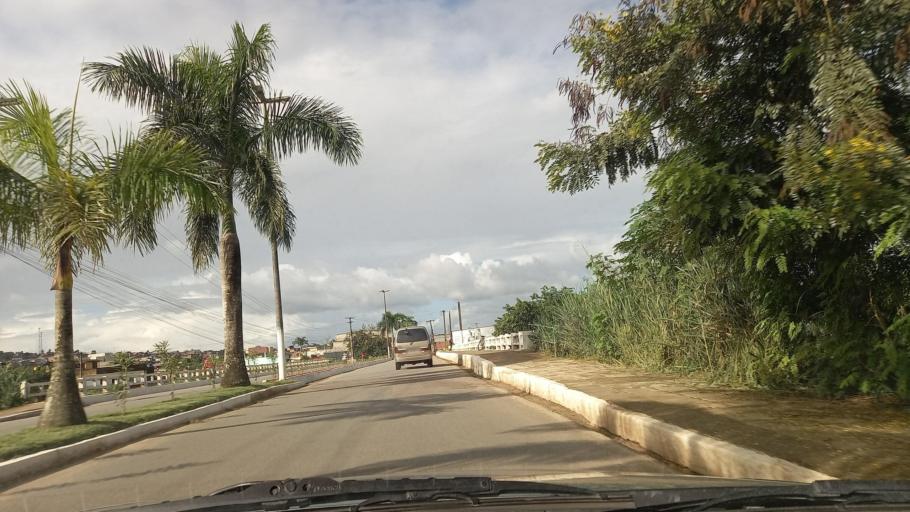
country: BR
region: Pernambuco
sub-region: Palmares
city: Palmares
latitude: -8.6888
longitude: -35.6003
